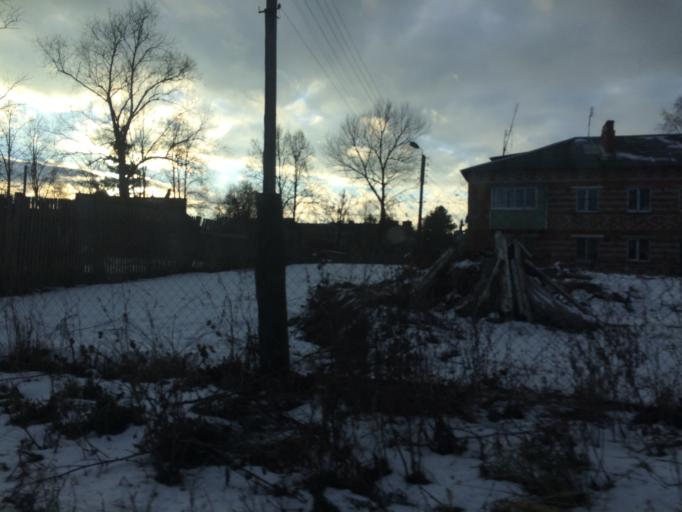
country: RU
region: Tula
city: Cherepet'
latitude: 54.1086
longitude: 36.3284
